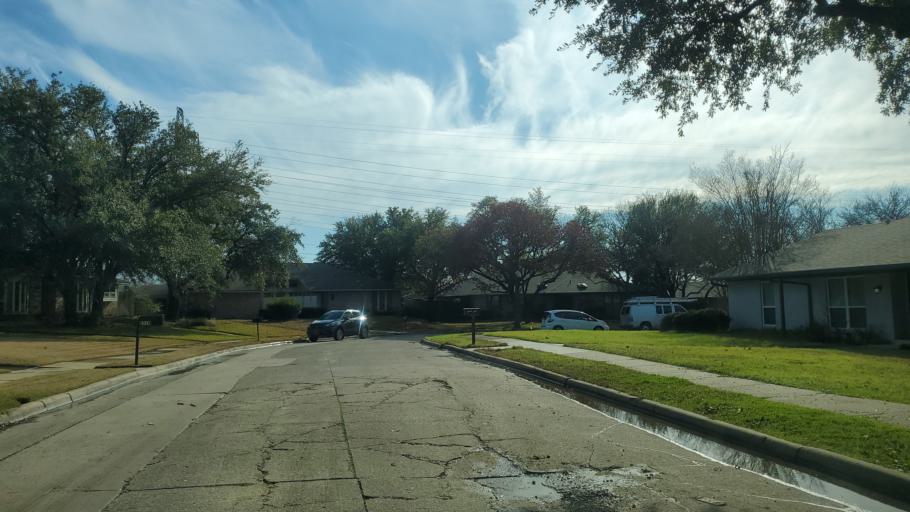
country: US
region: Texas
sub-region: Dallas County
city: Carrollton
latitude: 32.9785
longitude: -96.8949
